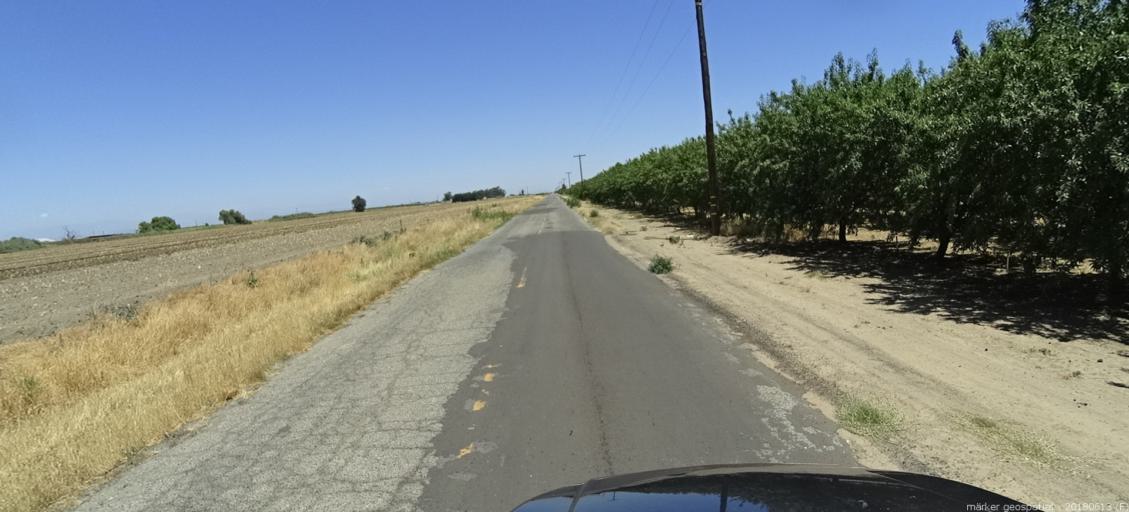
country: US
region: California
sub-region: Madera County
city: Fairmead
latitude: 36.9964
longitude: -120.1826
